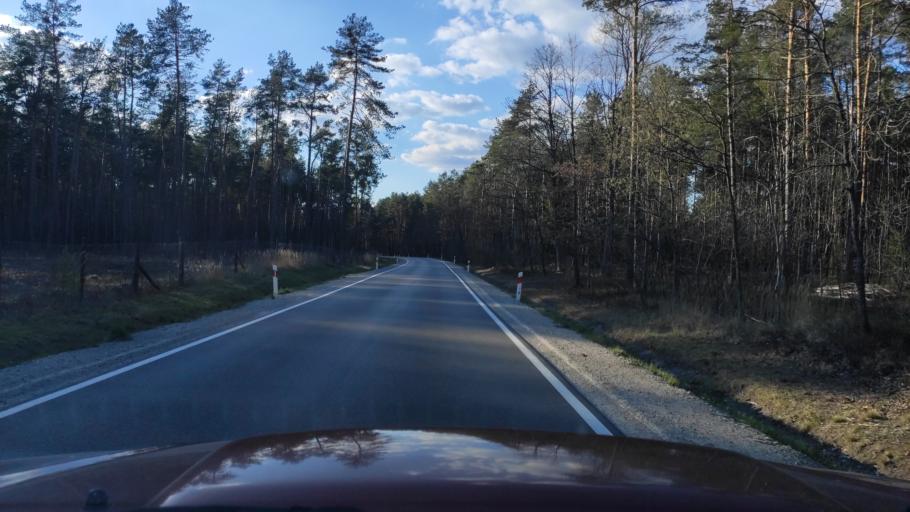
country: PL
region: Masovian Voivodeship
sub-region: Powiat zwolenski
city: Zwolen
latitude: 51.4020
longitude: 21.5361
